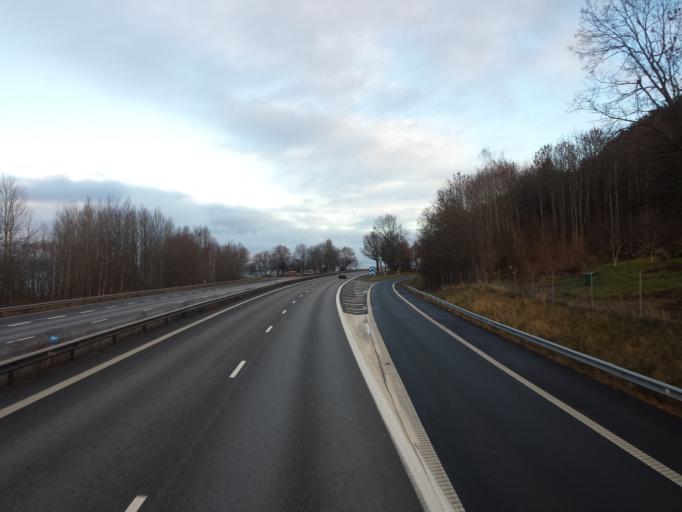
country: SE
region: Joenkoeping
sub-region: Jonkopings Kommun
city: Kaxholmen
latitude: 57.8500
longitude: 14.2666
